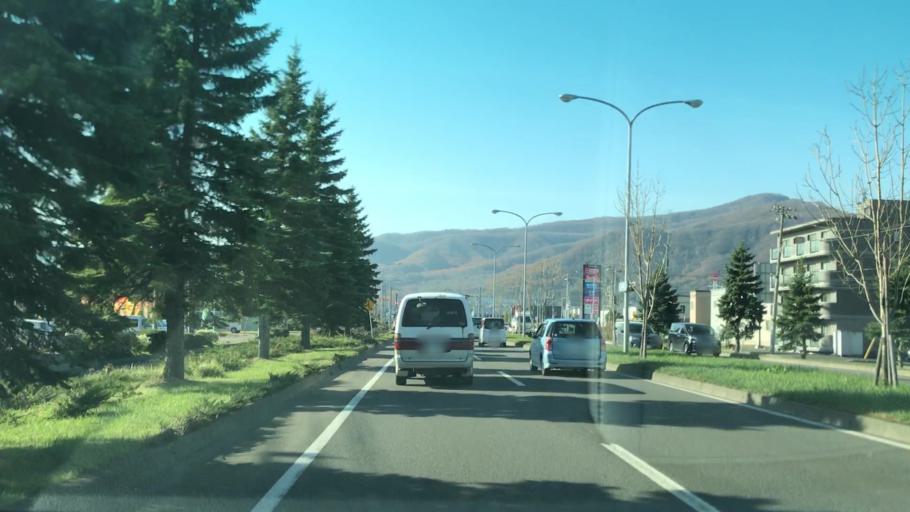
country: JP
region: Hokkaido
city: Sapporo
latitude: 43.1073
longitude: 141.2758
